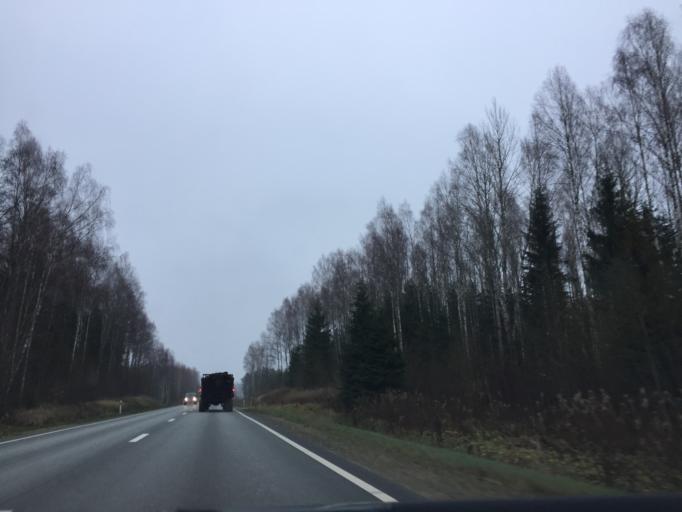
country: LV
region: Cesu Rajons
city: Cesis
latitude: 57.4299
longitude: 25.1756
